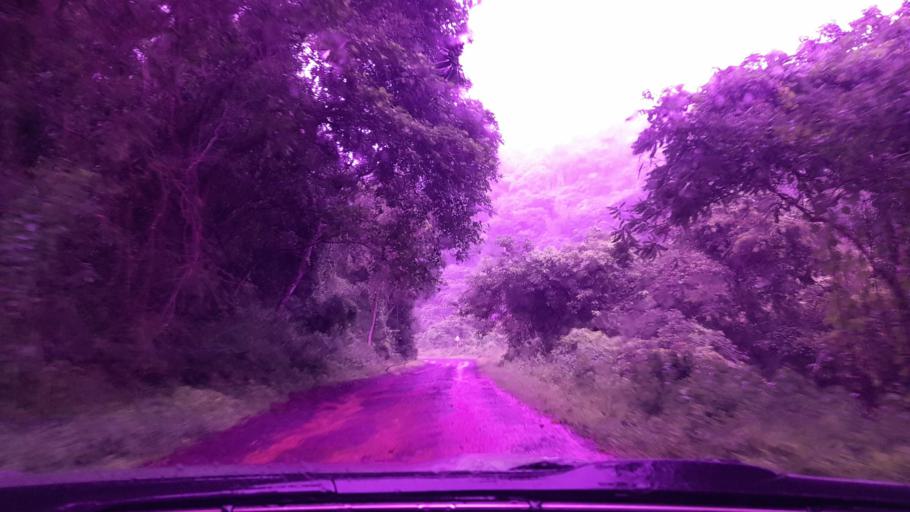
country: ET
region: Oromiya
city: Metu
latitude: 8.4803
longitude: 35.6470
